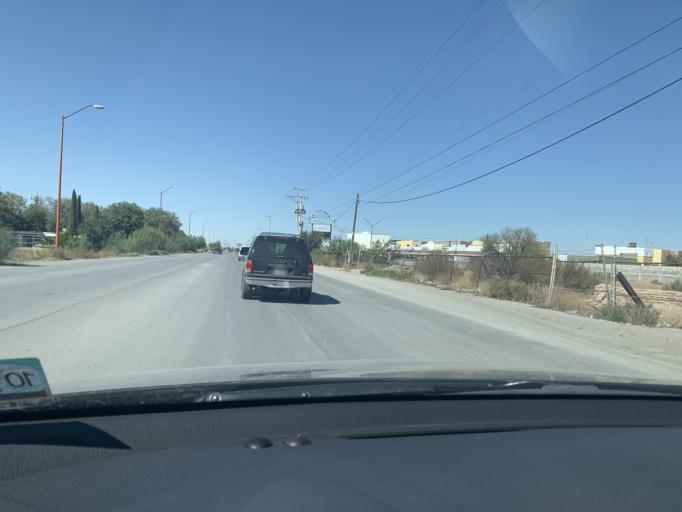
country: US
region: Texas
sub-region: El Paso County
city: Socorro
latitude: 31.6565
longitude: -106.3545
